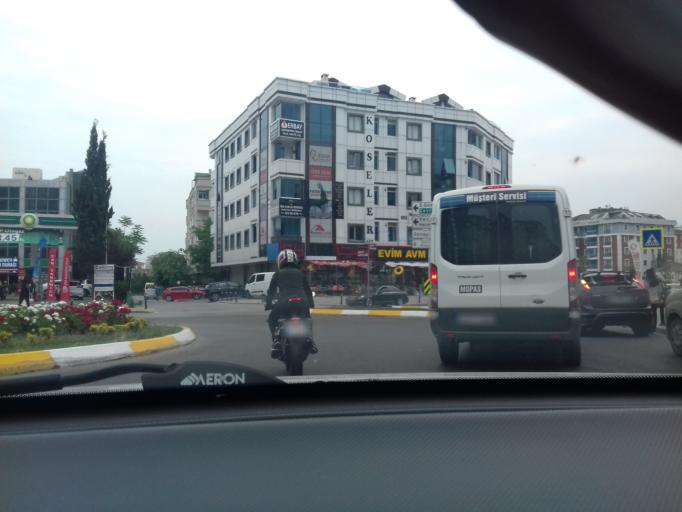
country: TR
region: Istanbul
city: Pendik
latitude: 40.9147
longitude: 29.3030
